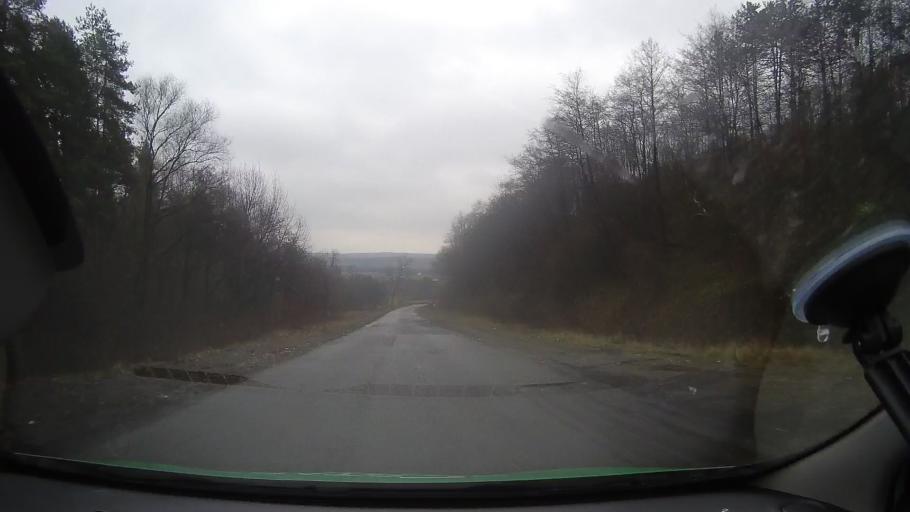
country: RO
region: Arad
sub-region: Comuna Halmagiu
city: Halmagiu
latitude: 46.2785
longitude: 22.5904
